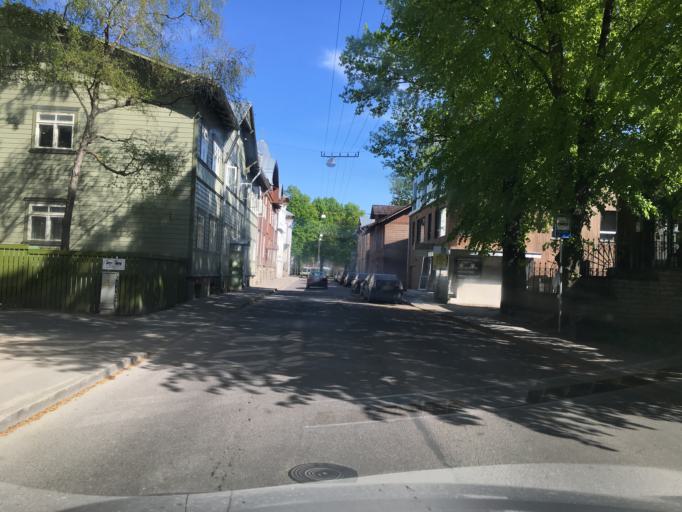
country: EE
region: Harju
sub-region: Tallinna linn
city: Tallinn
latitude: 59.4438
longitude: 24.7409
